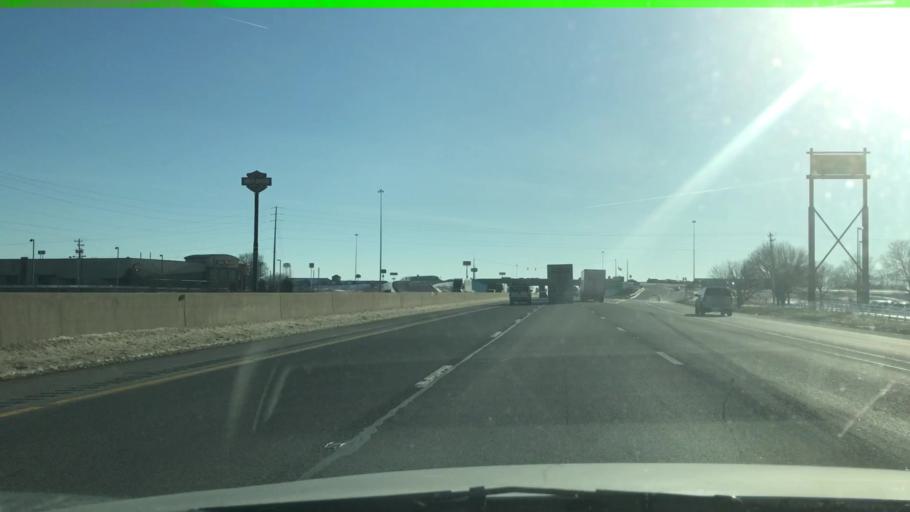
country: US
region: Kentucky
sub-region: Warren County
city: Plano
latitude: 36.9386
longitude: -86.4160
